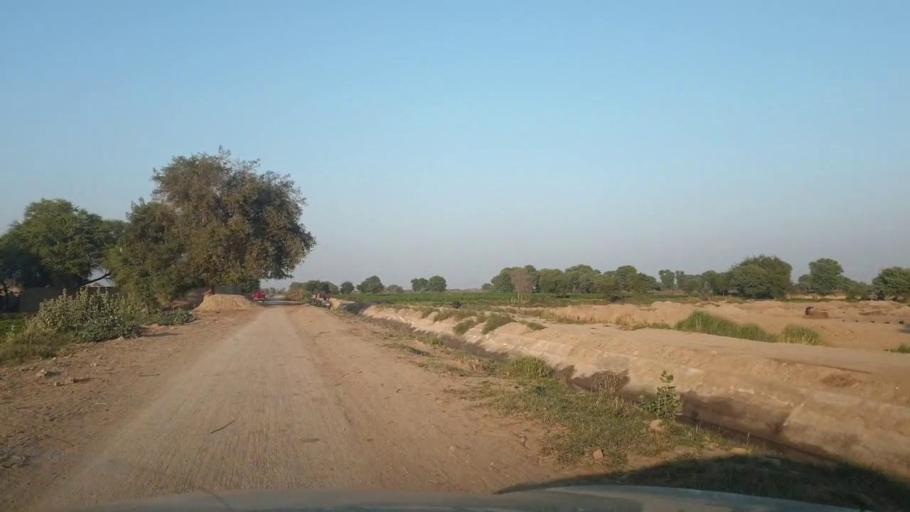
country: PK
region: Sindh
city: Bhan
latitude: 26.5500
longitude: 67.7391
